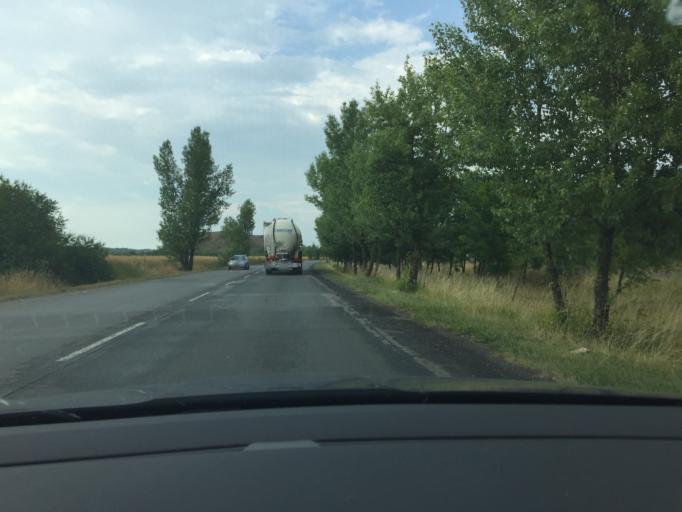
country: CZ
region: Central Bohemia
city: Kralupy nad Vltavou
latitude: 50.2564
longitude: 14.3186
